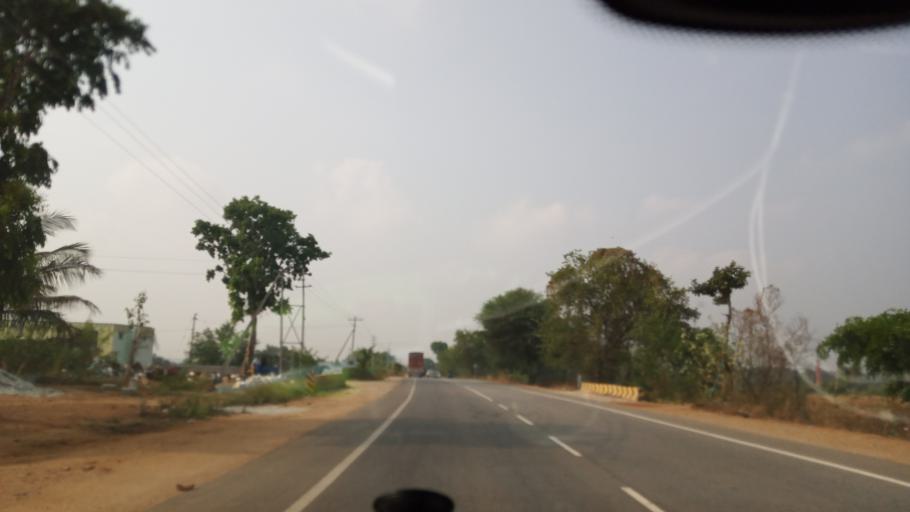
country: IN
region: Karnataka
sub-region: Mandya
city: Nagamangala
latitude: 12.7967
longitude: 76.7511
